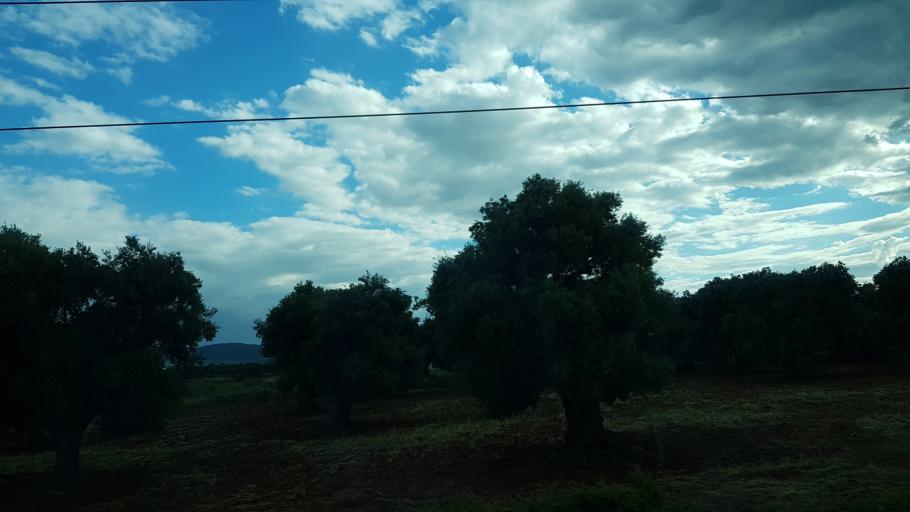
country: IT
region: Apulia
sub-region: Provincia di Brindisi
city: Pezze di Greco
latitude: 40.8406
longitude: 17.4049
